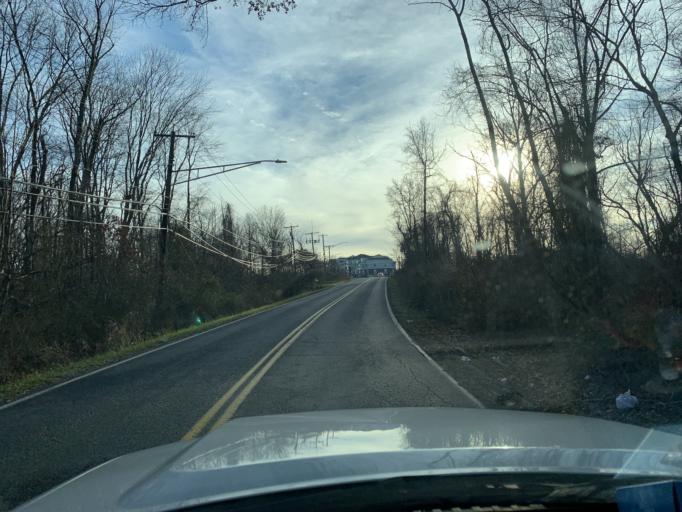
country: US
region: Maryland
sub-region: Anne Arundel County
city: Jessup
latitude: 39.1435
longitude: -76.7577
